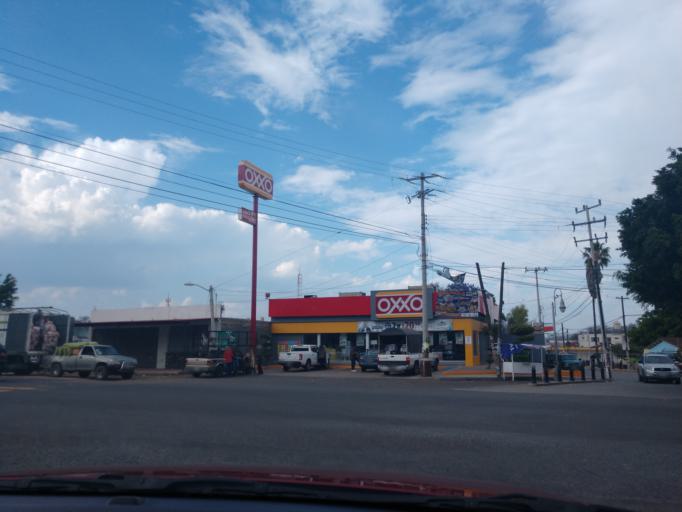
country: MX
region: Jalisco
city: Tizapan el Alto
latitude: 20.1528
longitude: -103.1860
